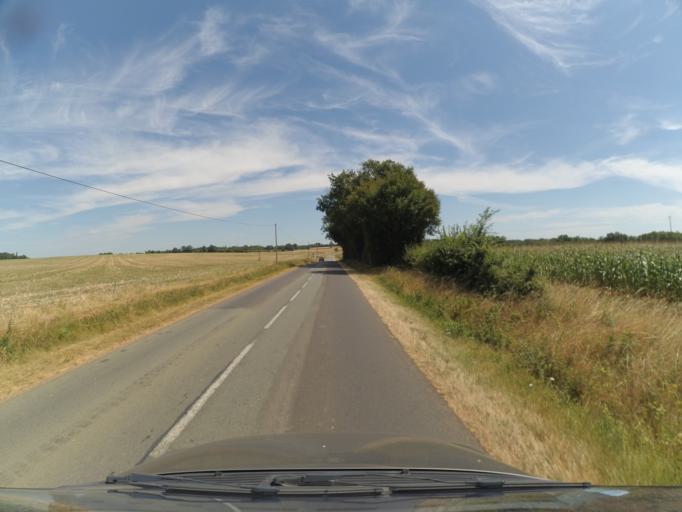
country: FR
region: Poitou-Charentes
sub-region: Departement de la Vienne
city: La Villedieu-du-Clain
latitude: 46.4101
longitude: 0.3308
